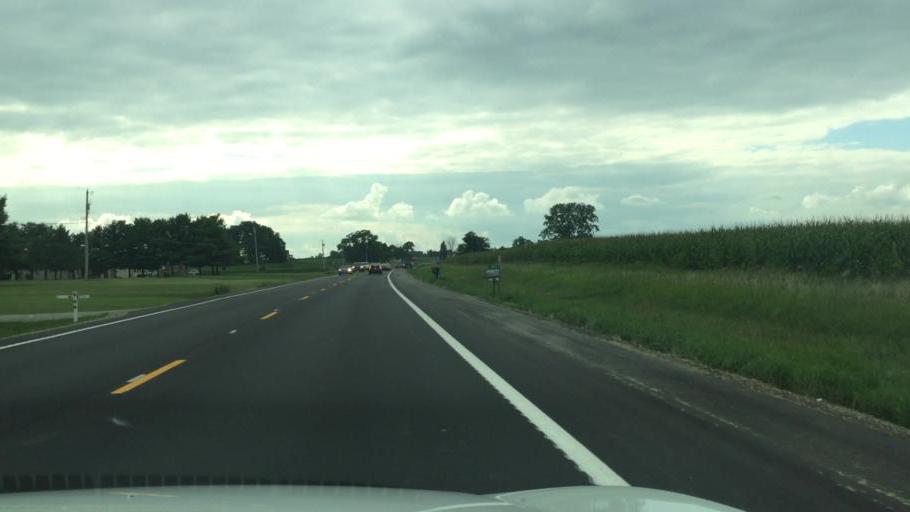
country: US
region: Ohio
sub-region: Champaign County
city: Urbana
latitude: 40.0854
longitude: -83.6763
